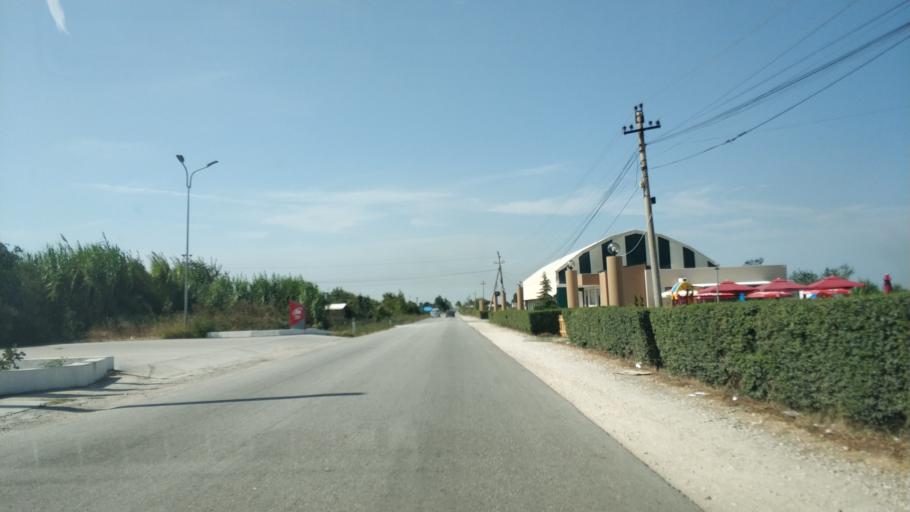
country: AL
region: Fier
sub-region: Rrethi i Fierit
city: Dermenas
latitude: 40.7379
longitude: 19.5170
